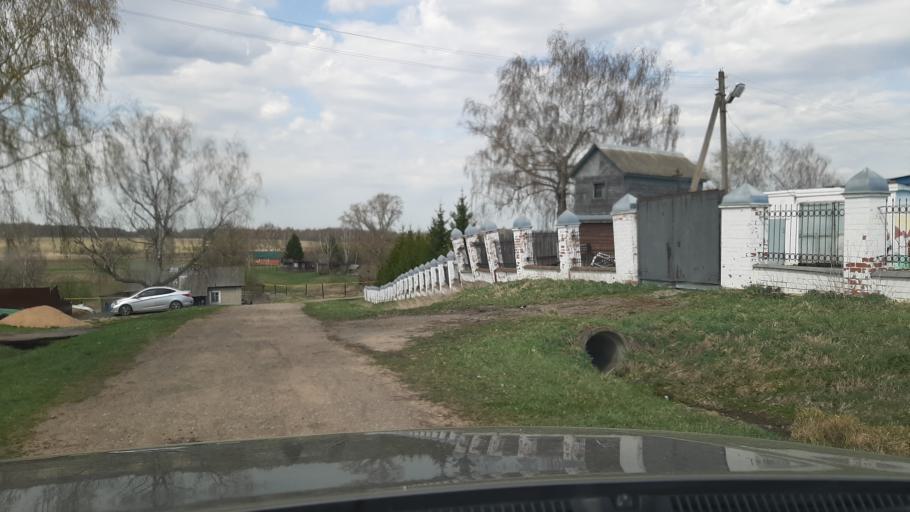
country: RU
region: Ivanovo
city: Privolzhsk
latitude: 57.3331
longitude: 41.2321
